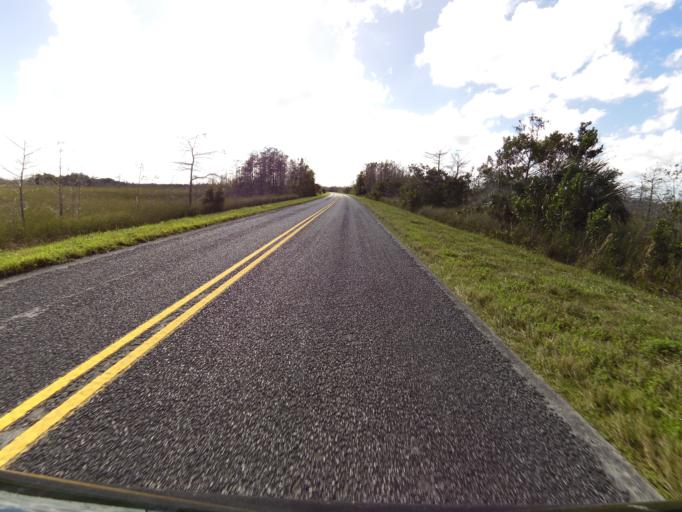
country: US
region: Florida
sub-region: Miami-Dade County
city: Florida City
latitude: 25.4236
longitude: -80.7755
